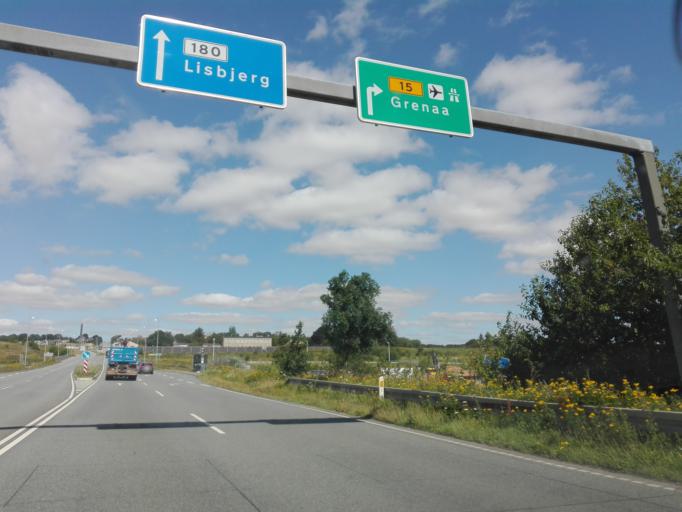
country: DK
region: Central Jutland
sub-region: Arhus Kommune
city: Trige
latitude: 56.2106
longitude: 10.1733
